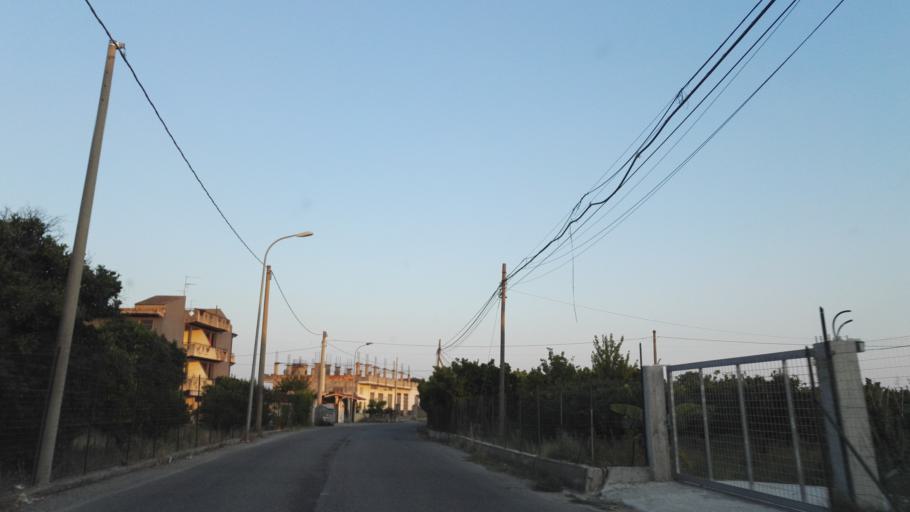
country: IT
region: Calabria
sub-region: Provincia di Reggio Calabria
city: Caulonia Marina
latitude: 38.3523
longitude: 16.4725
